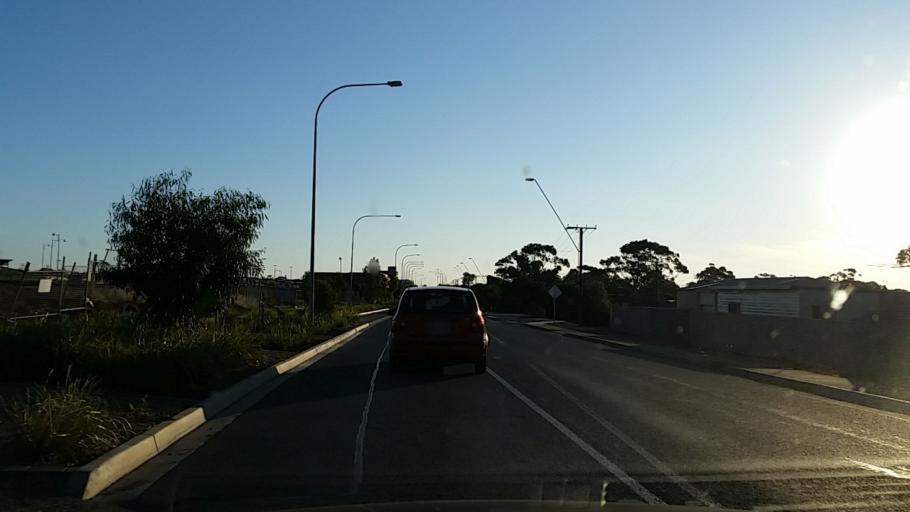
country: AU
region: South Australia
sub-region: Onkaparinga
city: Noarlunga
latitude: -35.1903
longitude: 138.4980
